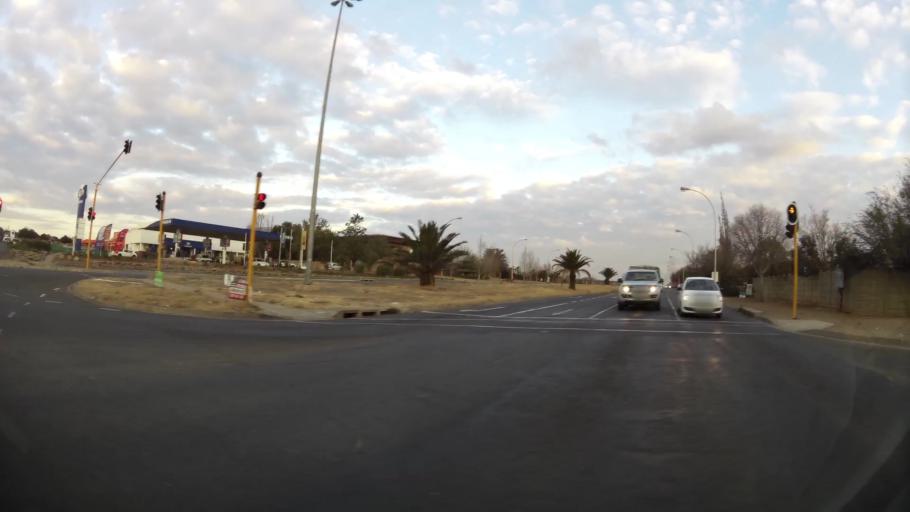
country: ZA
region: Orange Free State
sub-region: Mangaung Metropolitan Municipality
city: Bloemfontein
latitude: -29.1600
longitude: 26.1898
